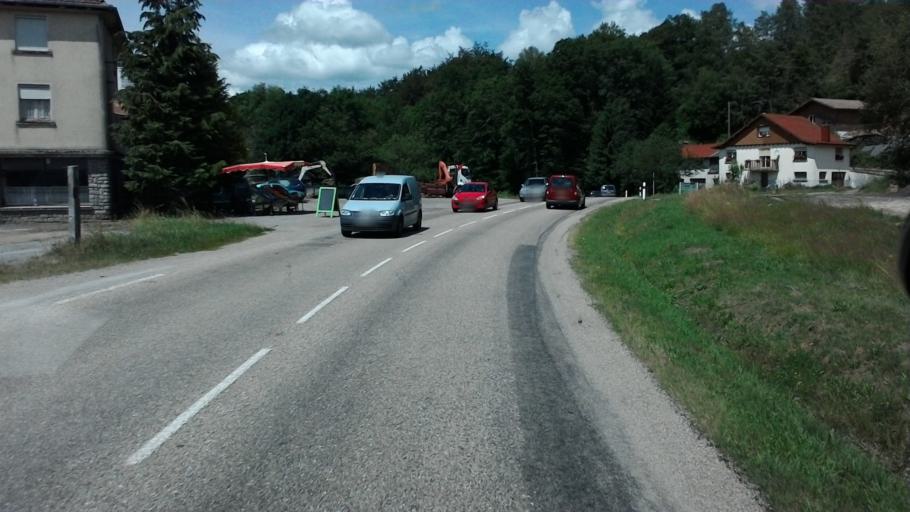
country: FR
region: Lorraine
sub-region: Departement des Vosges
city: Le Tholy
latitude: 48.0956
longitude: 6.7164
